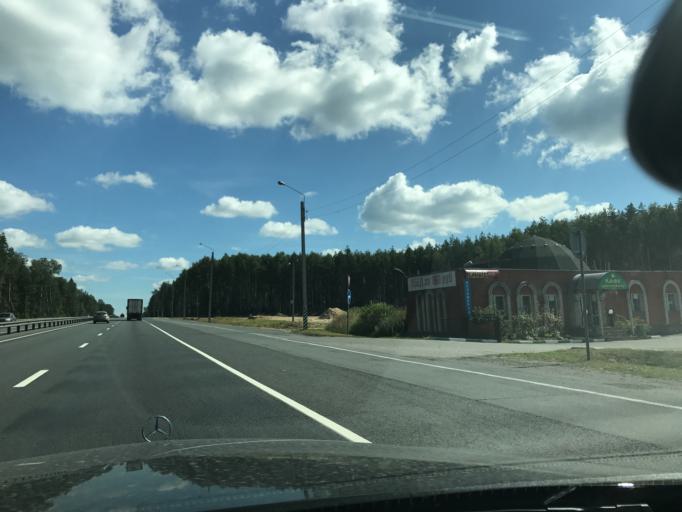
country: RU
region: Vladimir
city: Melekhovo
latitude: 56.2130
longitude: 41.3458
